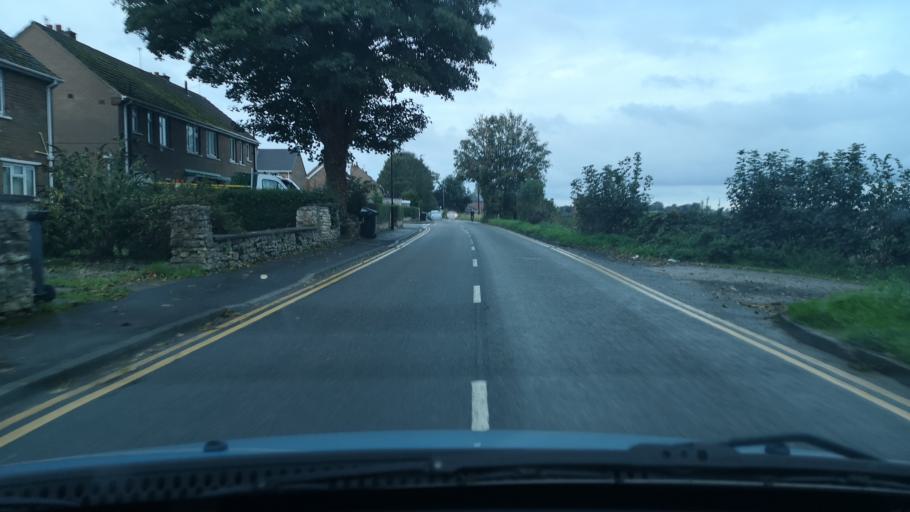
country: GB
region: England
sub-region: Doncaster
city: Campsall
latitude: 53.6227
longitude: -1.1735
